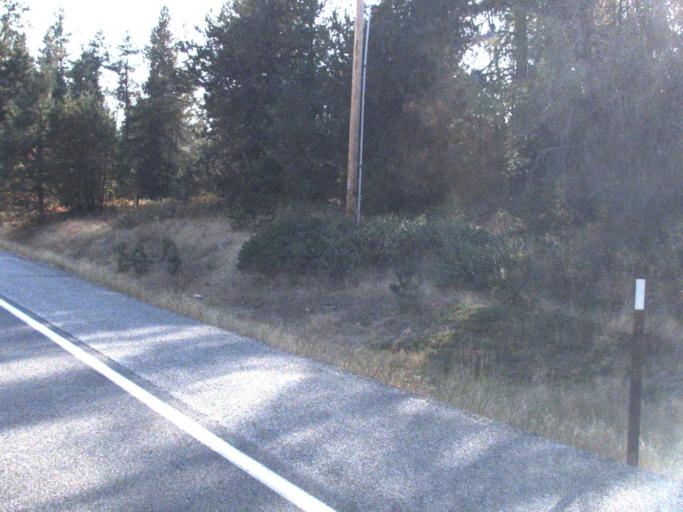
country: US
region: Washington
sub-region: Spokane County
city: Deer Park
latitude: 48.0377
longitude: -117.3495
